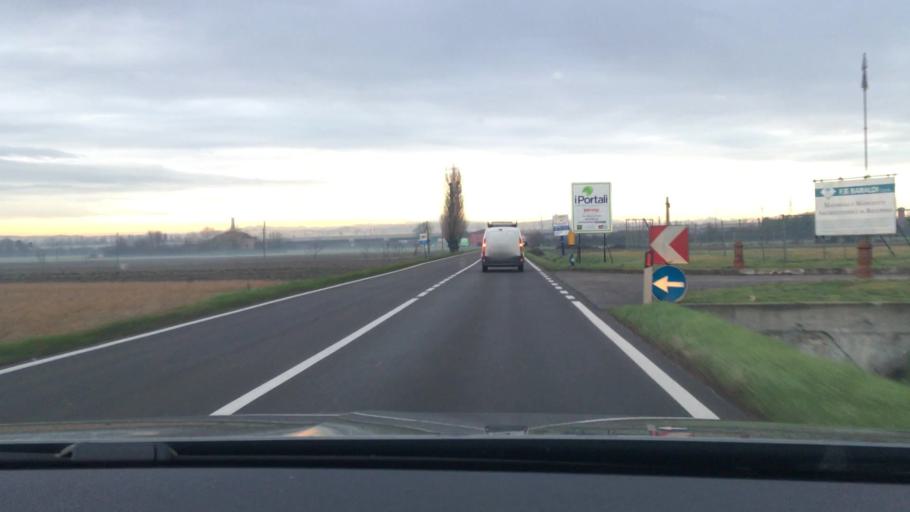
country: IT
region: Emilia-Romagna
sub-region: Provincia di Modena
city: Albareto
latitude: 44.6975
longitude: 10.9475
